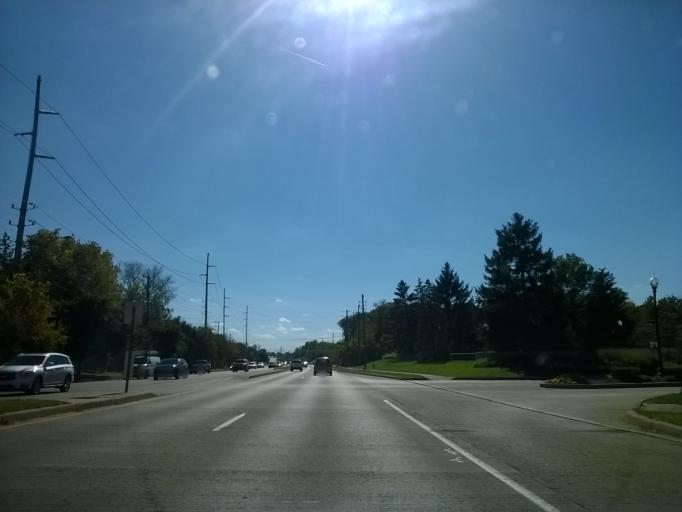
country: US
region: Indiana
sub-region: Hamilton County
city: Fishers
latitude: 39.9219
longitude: -86.0701
